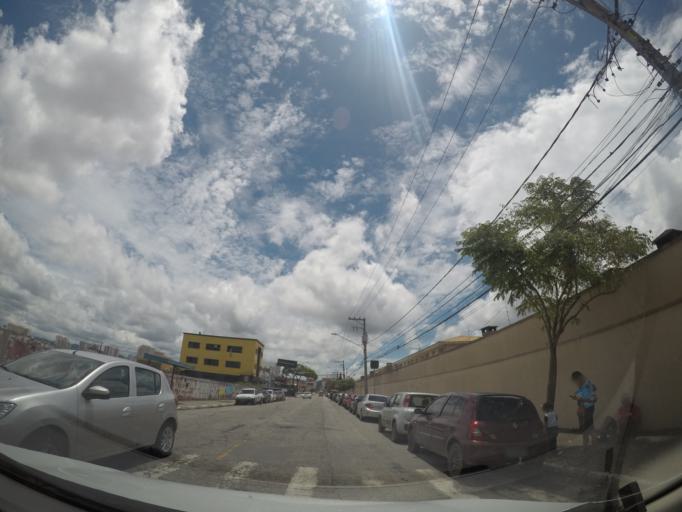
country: BR
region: Sao Paulo
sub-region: Guarulhos
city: Guarulhos
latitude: -23.4509
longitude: -46.5305
